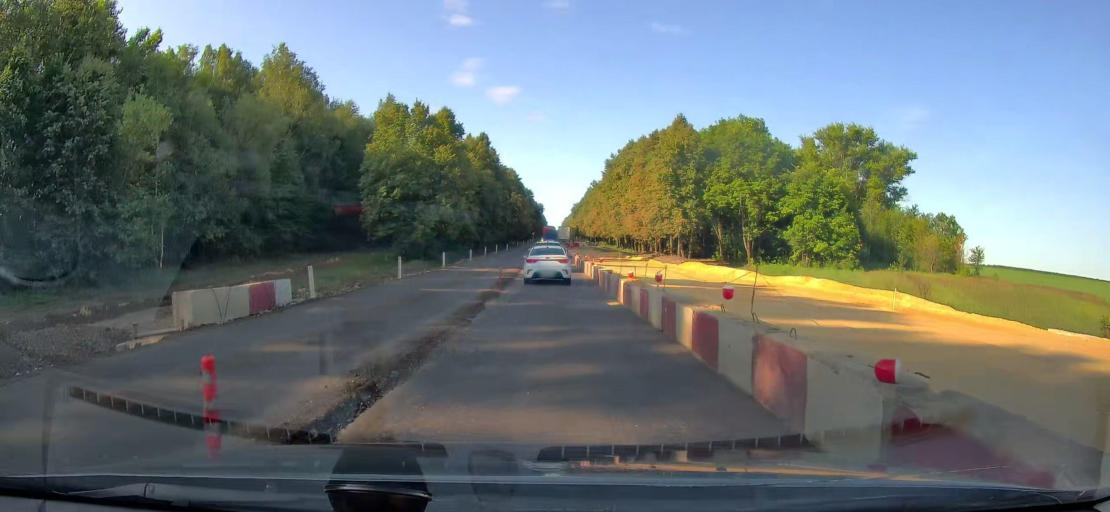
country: RU
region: Orjol
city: Spasskoye-Lutovinovo
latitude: 53.3667
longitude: 36.7291
